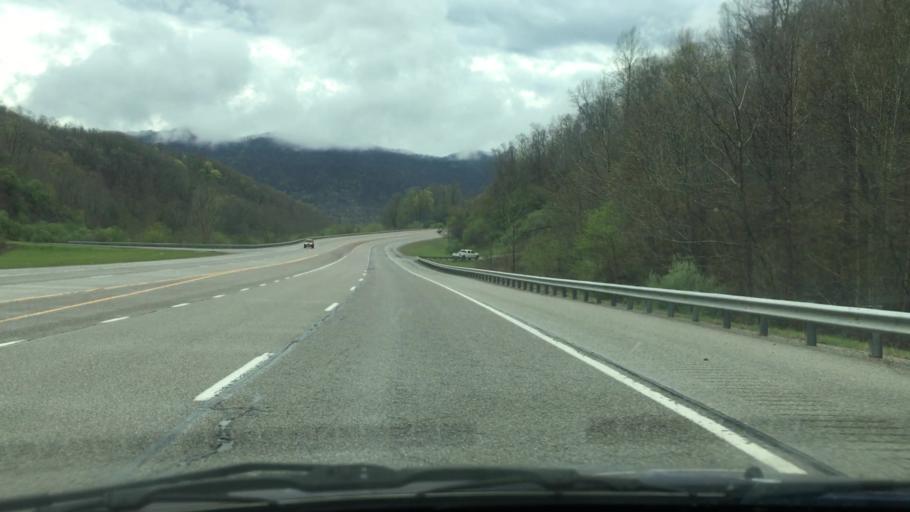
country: US
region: Kentucky
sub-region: Letcher County
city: Jenkins
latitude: 37.2049
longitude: -82.6235
